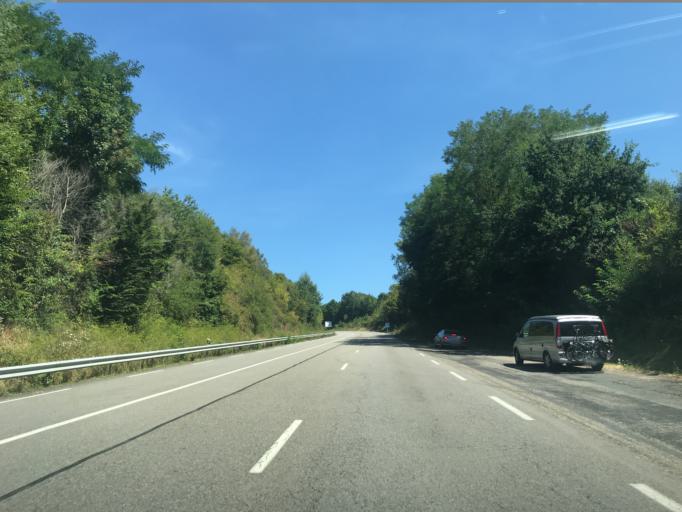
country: FR
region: Limousin
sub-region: Departement de la Correze
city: Tulle
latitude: 45.2799
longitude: 1.7938
